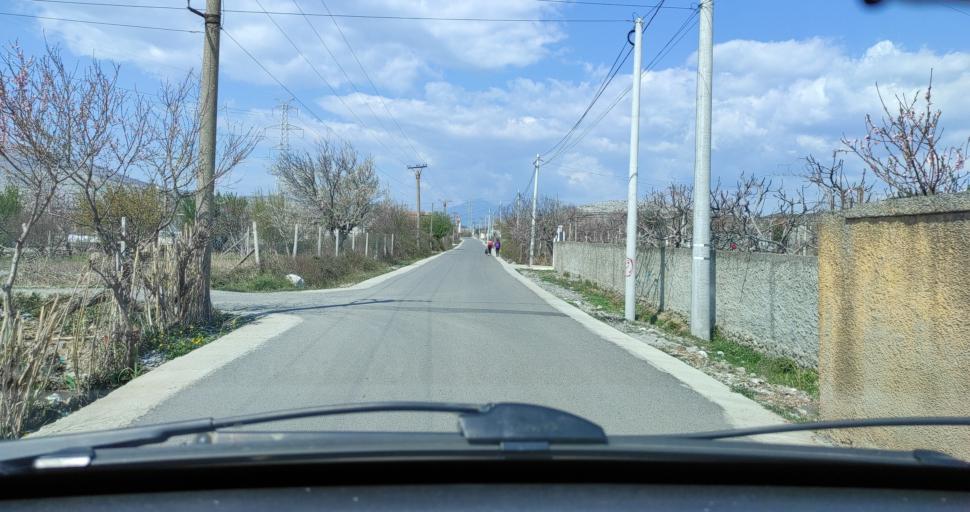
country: AL
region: Shkoder
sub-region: Rrethi i Shkodres
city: Vau i Dejes
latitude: 41.9995
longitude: 19.6429
